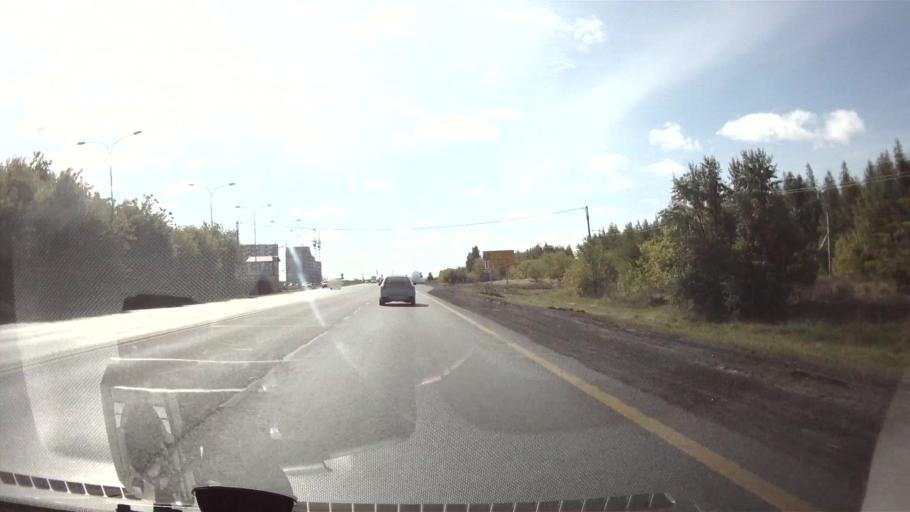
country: RU
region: Ulyanovsk
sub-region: Ulyanovskiy Rayon
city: Ulyanovsk
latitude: 54.2874
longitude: 48.2561
